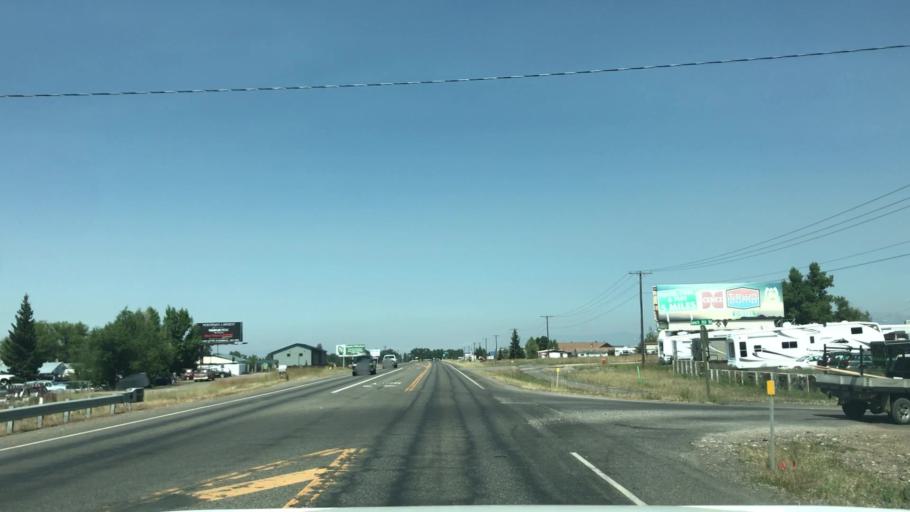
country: US
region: Montana
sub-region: Gallatin County
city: Four Corners
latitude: 45.5982
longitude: -111.1965
